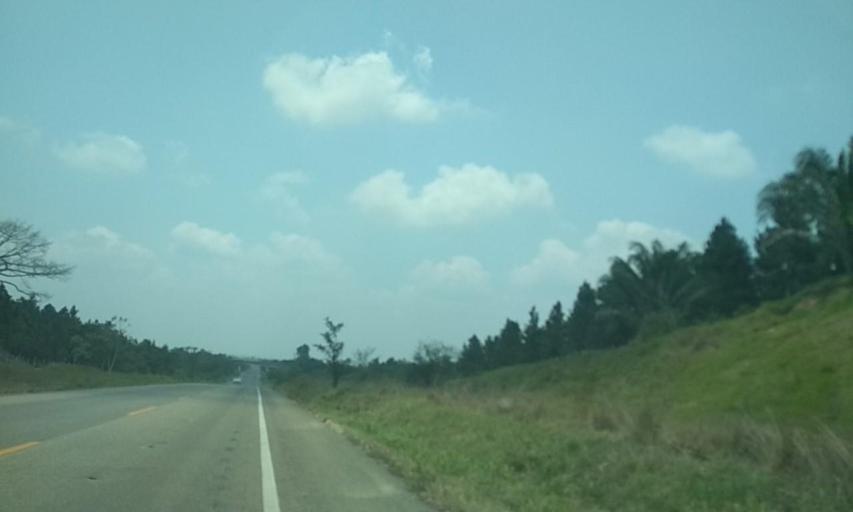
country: MX
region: Tabasco
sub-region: Huimanguillo
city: Francisco Rueda
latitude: 17.7541
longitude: -94.0001
